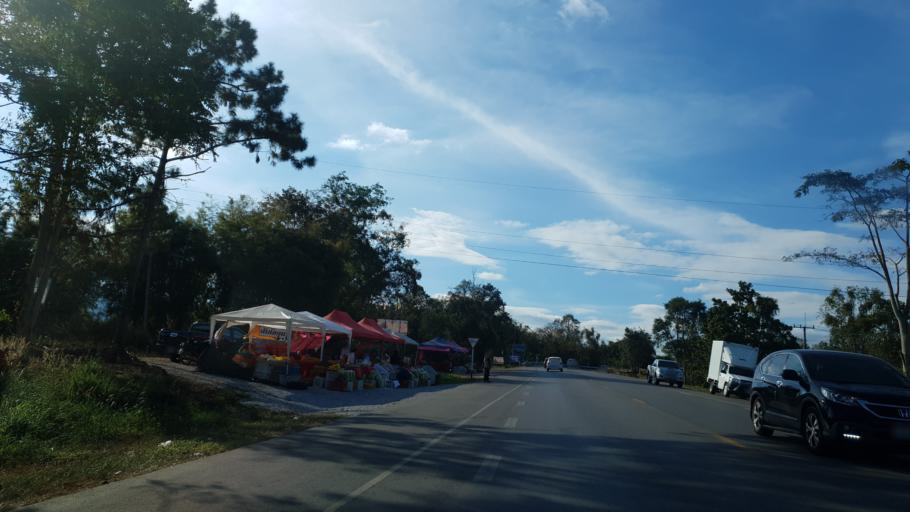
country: TH
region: Loei
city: Phu Ruea
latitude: 17.4422
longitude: 101.4697
